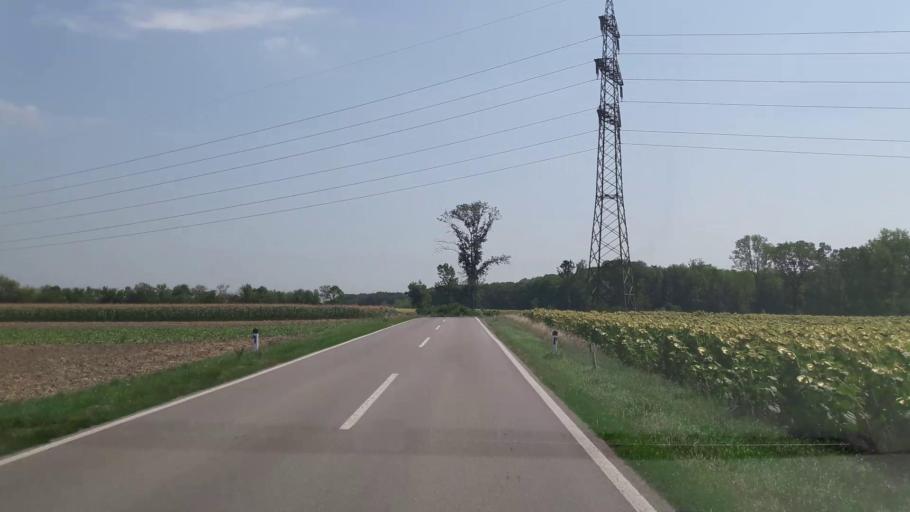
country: AT
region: Lower Austria
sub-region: Politischer Bezirk Bruck an der Leitha
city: Gotzendorf an der Leitha
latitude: 48.0201
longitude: 16.6026
